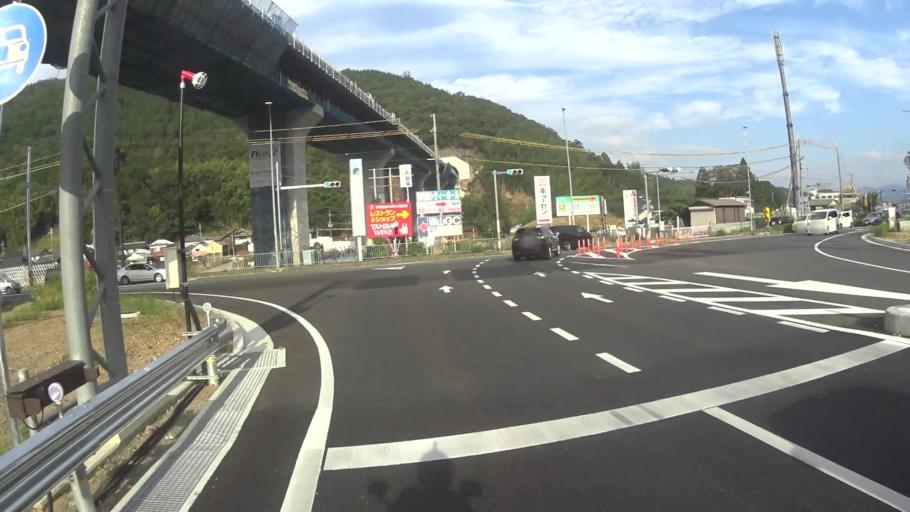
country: JP
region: Kyoto
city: Kameoka
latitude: 35.1488
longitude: 135.4290
